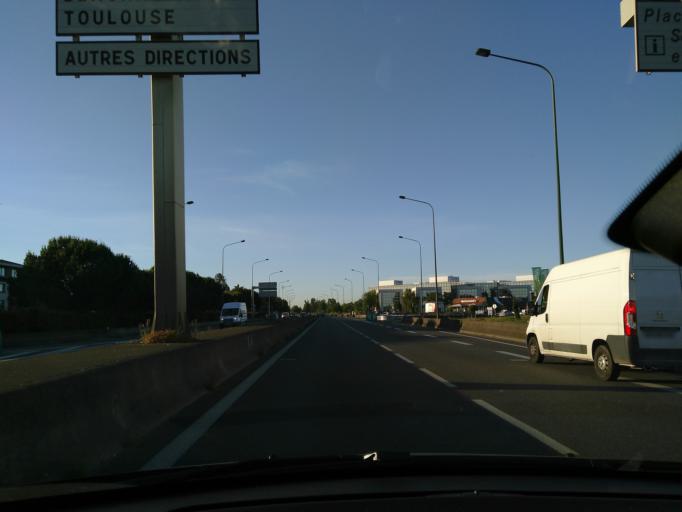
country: FR
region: Midi-Pyrenees
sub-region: Departement de la Haute-Garonne
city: Blagnac
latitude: 43.6392
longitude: 1.3760
